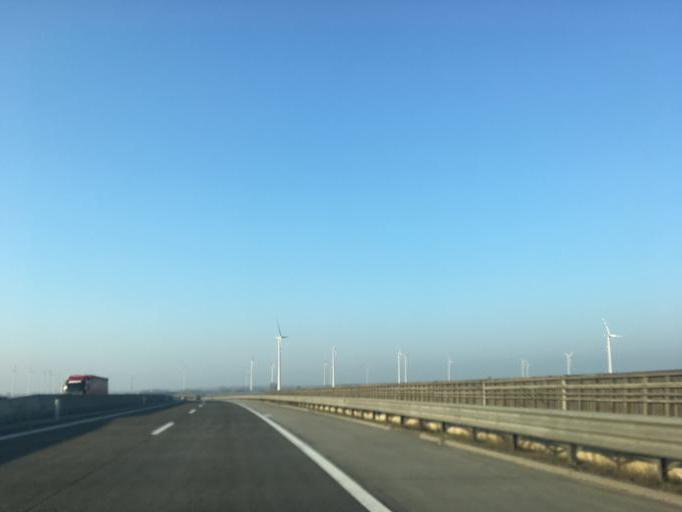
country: AT
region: Burgenland
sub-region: Politischer Bezirk Neusiedl am See
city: Pama
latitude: 48.0734
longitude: 17.0154
